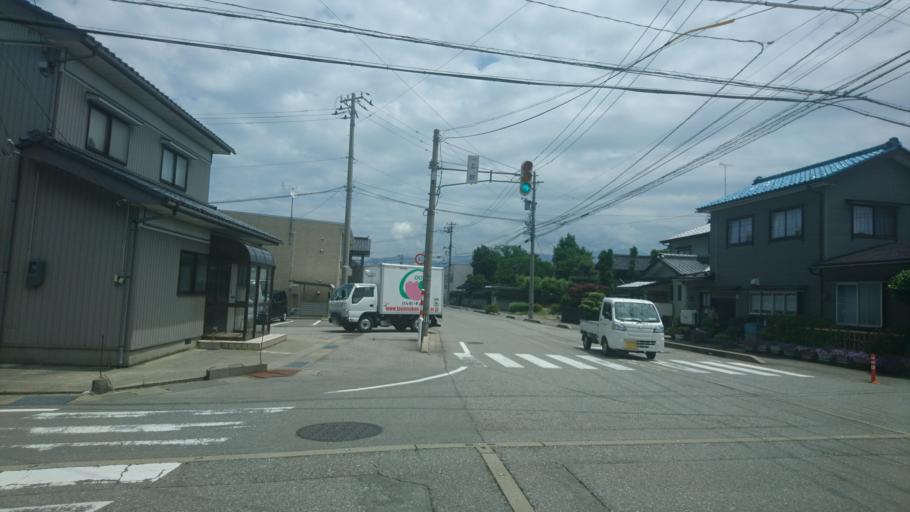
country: JP
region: Toyama
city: Nyuzen
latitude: 36.9335
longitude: 137.4974
